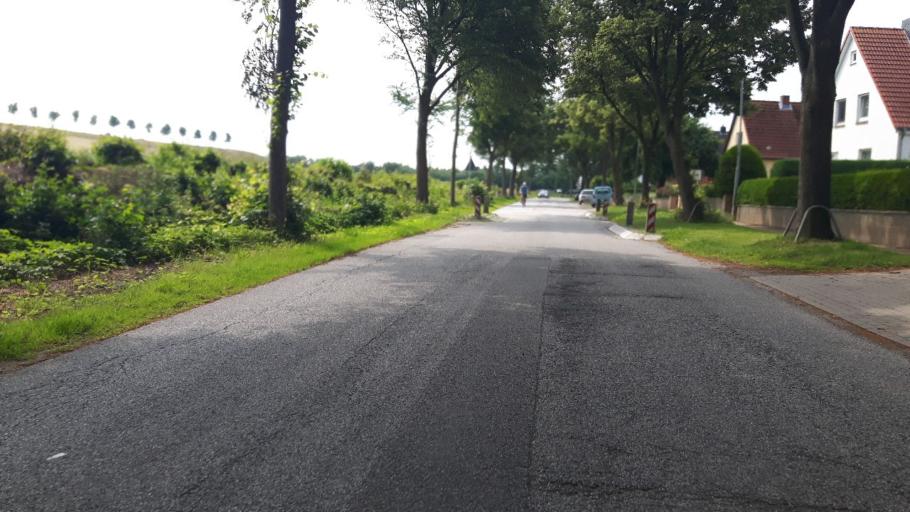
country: DE
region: Schleswig-Holstein
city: Travemuende
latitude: 53.9407
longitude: 10.8436
